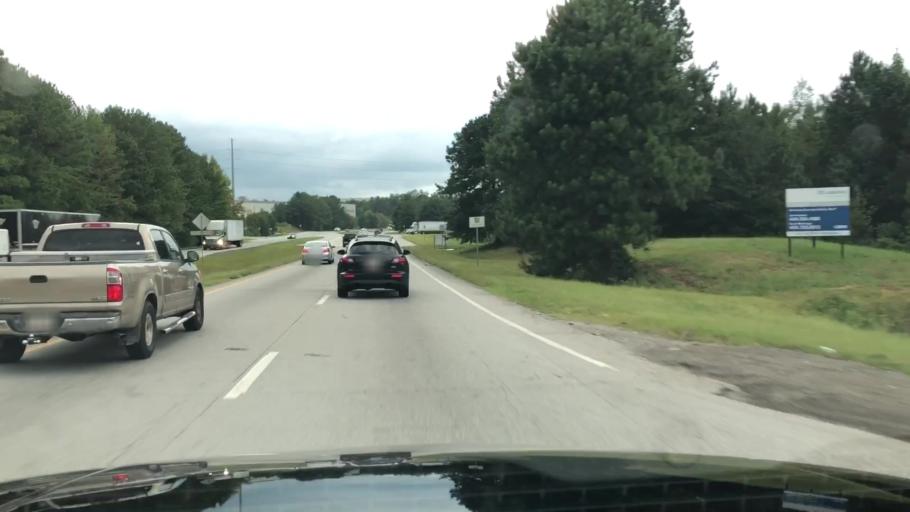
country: US
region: Georgia
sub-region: Cobb County
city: Mableton
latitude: 33.7404
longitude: -84.5862
